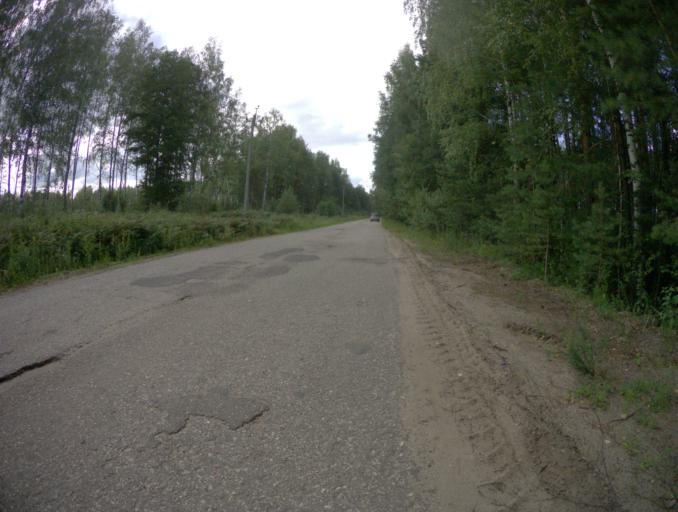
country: RU
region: Vladimir
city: Sobinka
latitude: 55.9682
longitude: 40.0552
